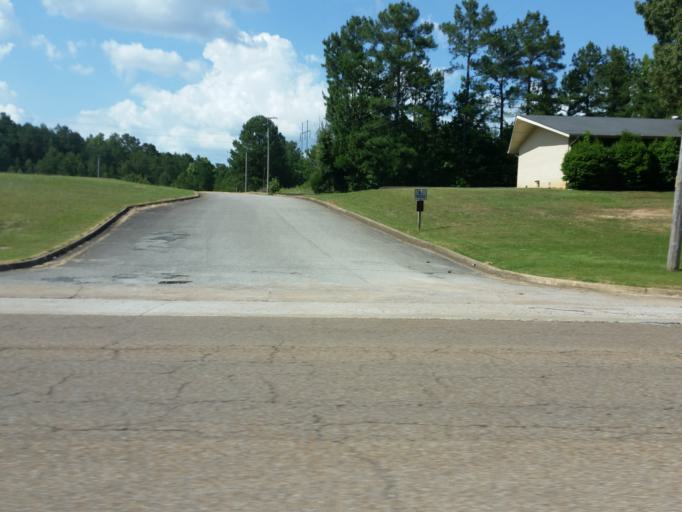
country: US
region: Tennessee
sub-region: Henderson County
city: Lexington
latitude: 35.6413
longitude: -88.3755
